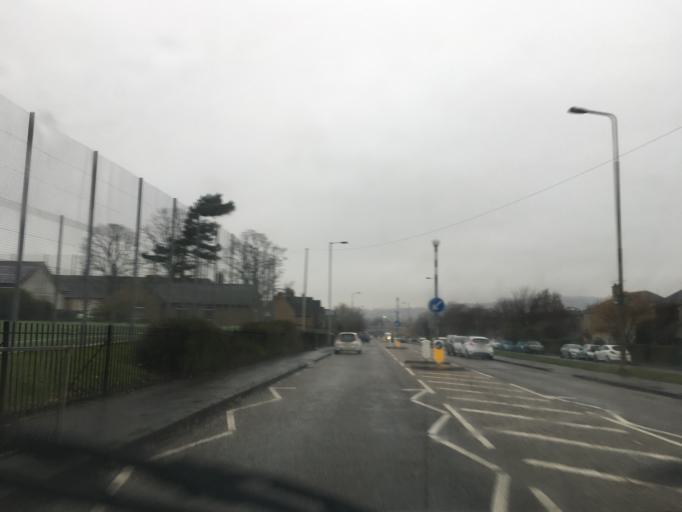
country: GB
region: Scotland
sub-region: Edinburgh
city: Colinton
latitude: 55.9289
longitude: -3.2722
